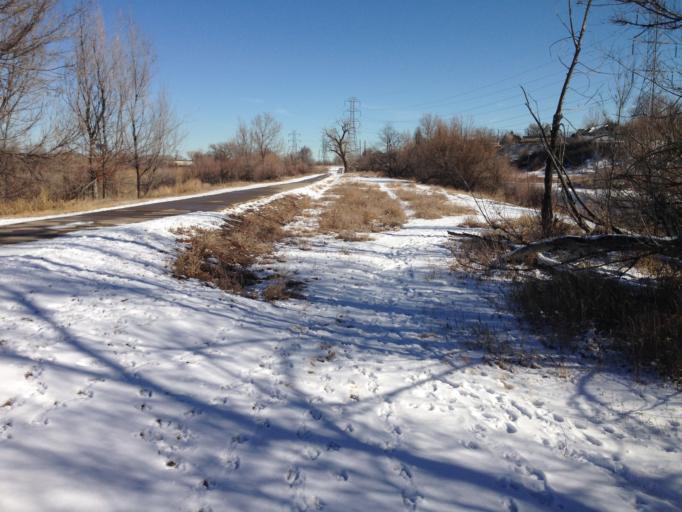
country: US
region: Colorado
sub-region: Adams County
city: Berkley
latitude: 39.7962
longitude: -105.0386
